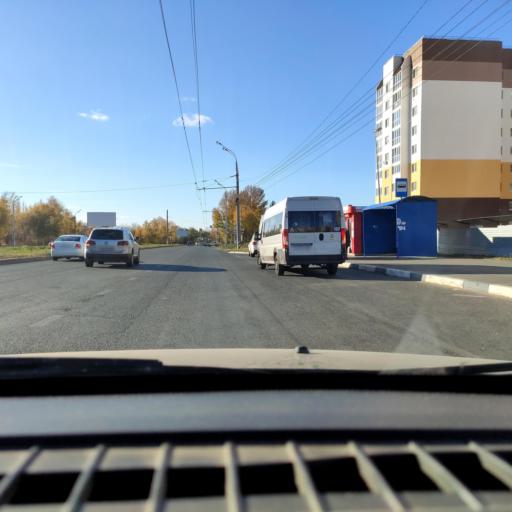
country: RU
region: Samara
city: Tol'yatti
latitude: 53.5001
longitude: 49.2712
